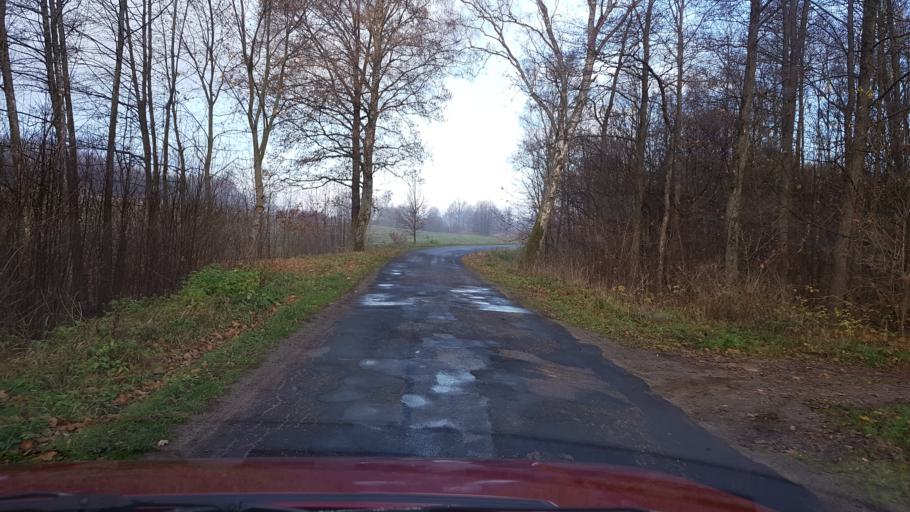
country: PL
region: West Pomeranian Voivodeship
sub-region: Powiat bialogardzki
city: Tychowo
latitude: 53.9860
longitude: 16.3235
